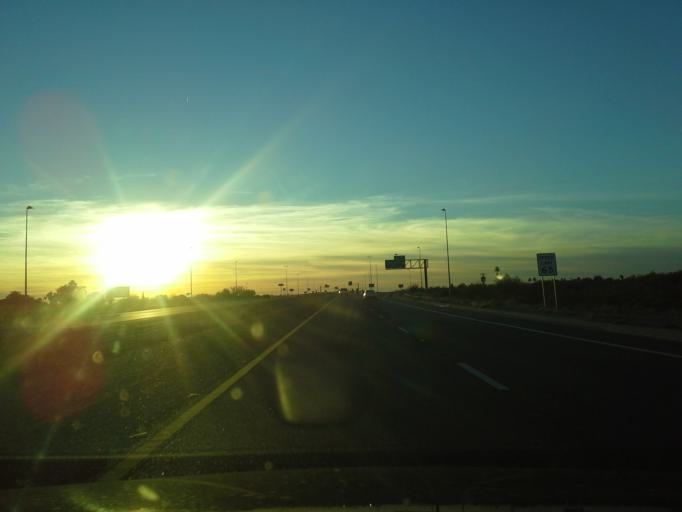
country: US
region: Arizona
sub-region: Pinal County
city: Apache Junction
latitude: 33.3867
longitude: -111.5212
